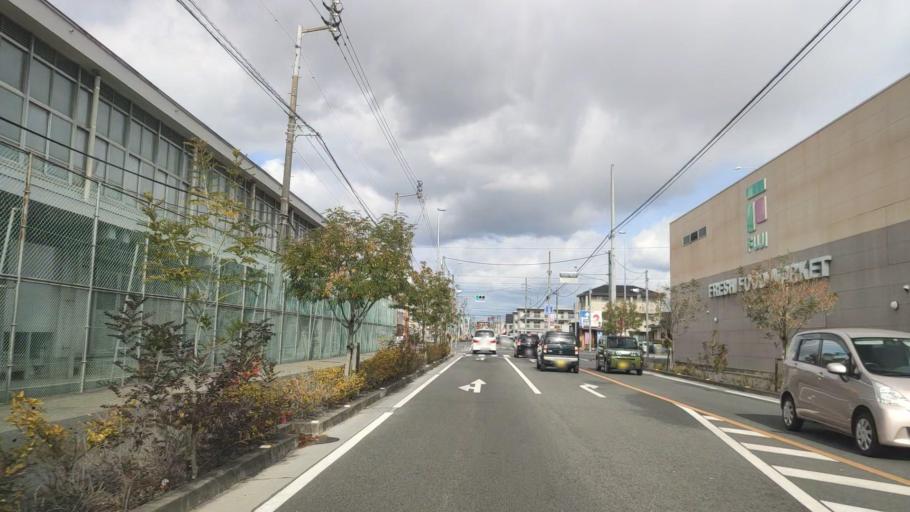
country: JP
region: Ehime
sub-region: Shikoku-chuo Shi
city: Matsuyama
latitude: 33.8112
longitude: 132.7608
